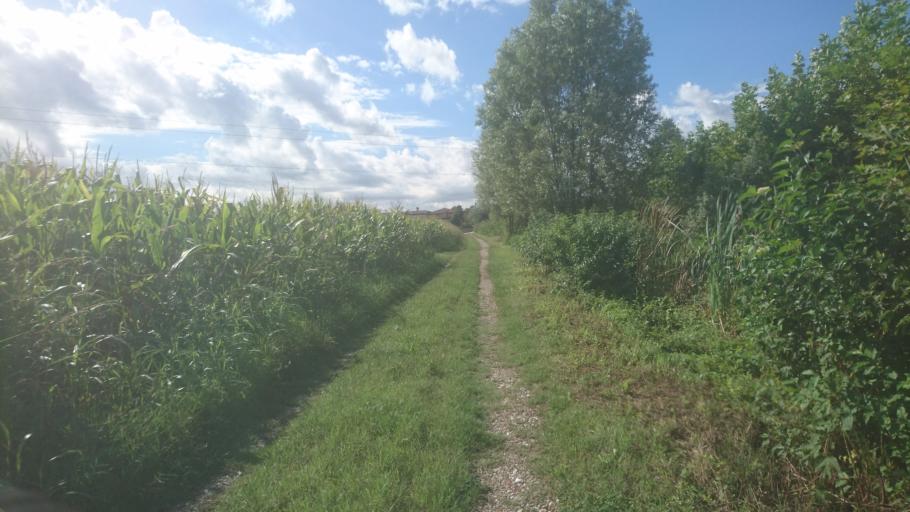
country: IT
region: Veneto
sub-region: Provincia di Venezia
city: Fosso
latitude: 45.3913
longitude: 12.0429
